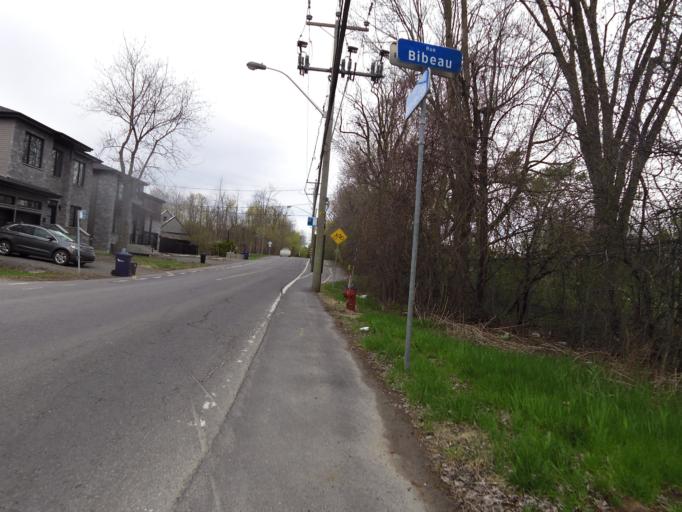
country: CA
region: Quebec
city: Dollard-Des Ormeaux
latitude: 45.5220
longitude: -73.8406
